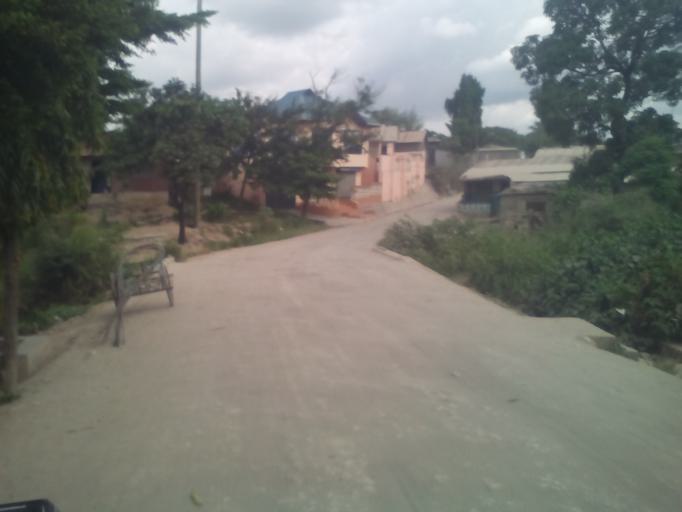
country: TZ
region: Dar es Salaam
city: Dar es Salaam
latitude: -6.8580
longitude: 39.2453
